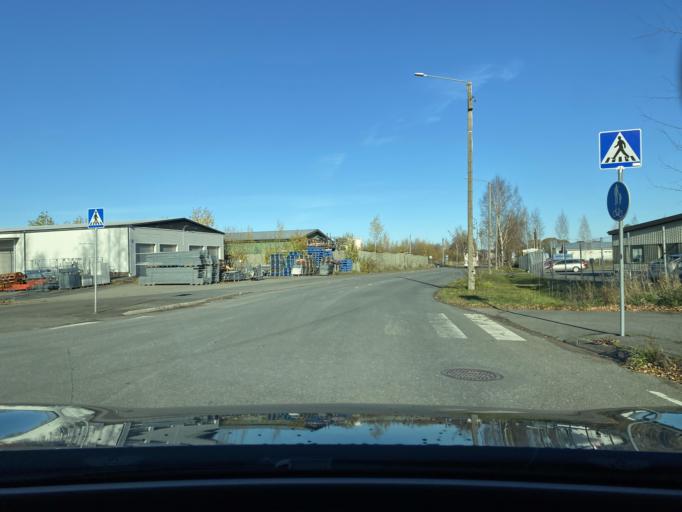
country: FI
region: Haeme
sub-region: Haemeenlinna
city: Haemeenlinna
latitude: 61.0131
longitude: 24.4059
